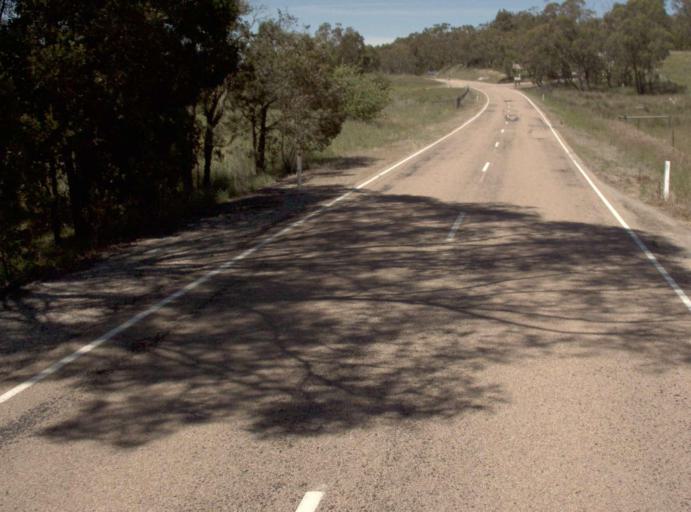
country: AU
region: Victoria
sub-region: East Gippsland
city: Lakes Entrance
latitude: -37.1850
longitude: 148.2692
